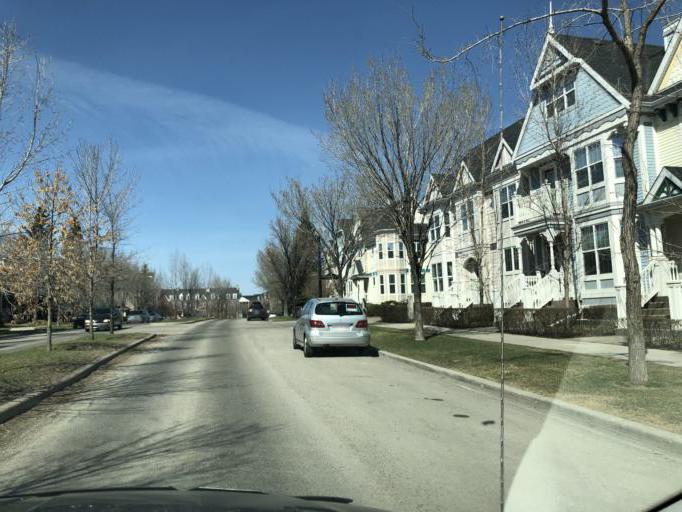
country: CA
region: Alberta
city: Calgary
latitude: 51.0197
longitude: -114.1139
